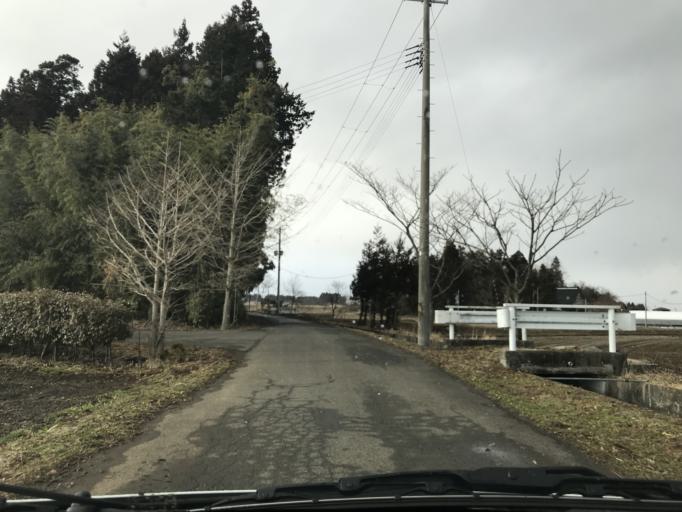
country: JP
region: Iwate
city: Mizusawa
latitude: 39.0830
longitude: 141.0410
